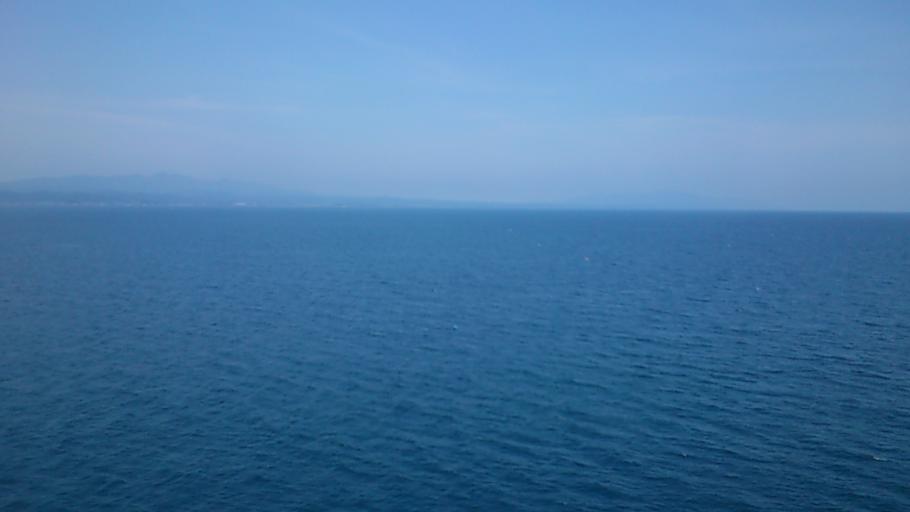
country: JP
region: Aomori
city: Aomori Shi
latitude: 40.8599
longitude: 140.7326
